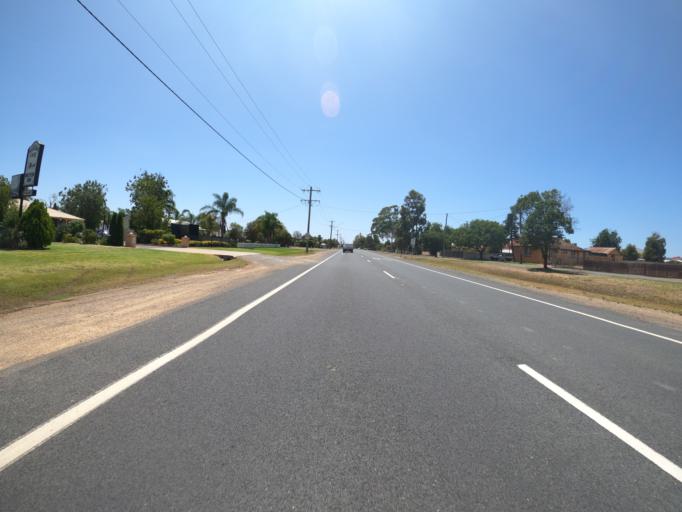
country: AU
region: New South Wales
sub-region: Corowa Shire
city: Mulwala
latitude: -35.9818
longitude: 146.0140
